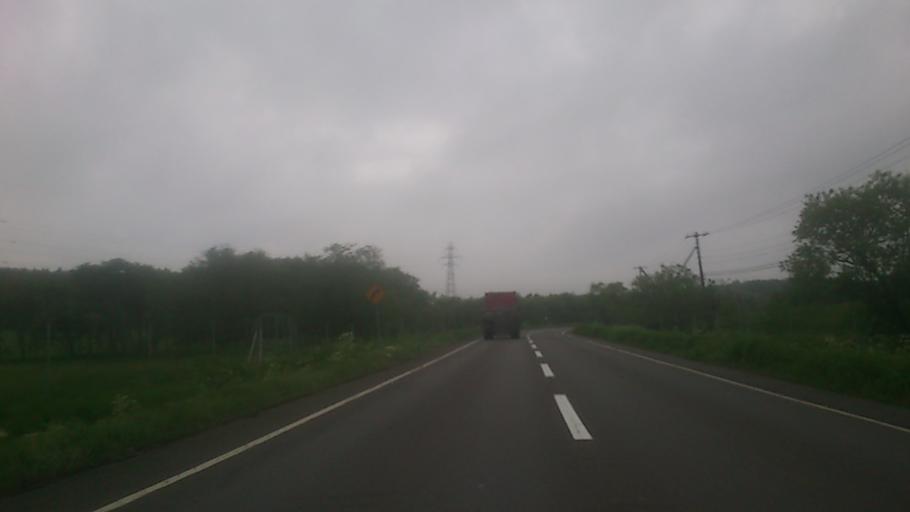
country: JP
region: Hokkaido
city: Kushiro
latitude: 43.0094
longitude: 144.6475
